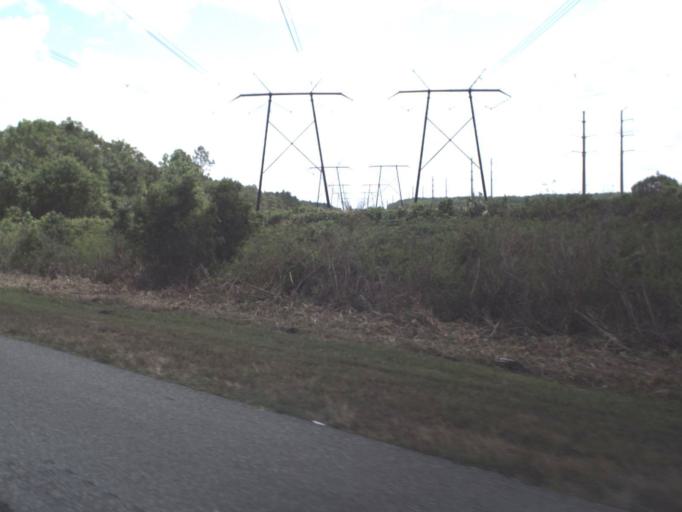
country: US
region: Florida
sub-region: Orange County
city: Wedgefield
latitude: 28.4524
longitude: -81.0104
